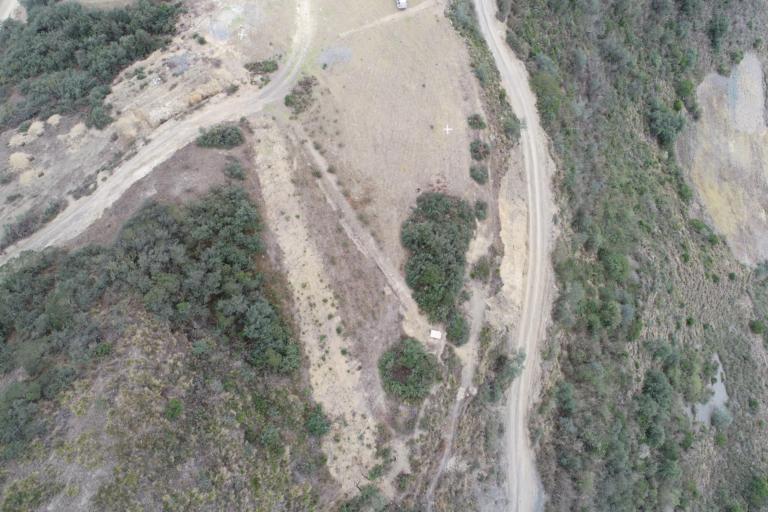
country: BO
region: La Paz
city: Sorata
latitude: -15.6186
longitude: -68.7009
